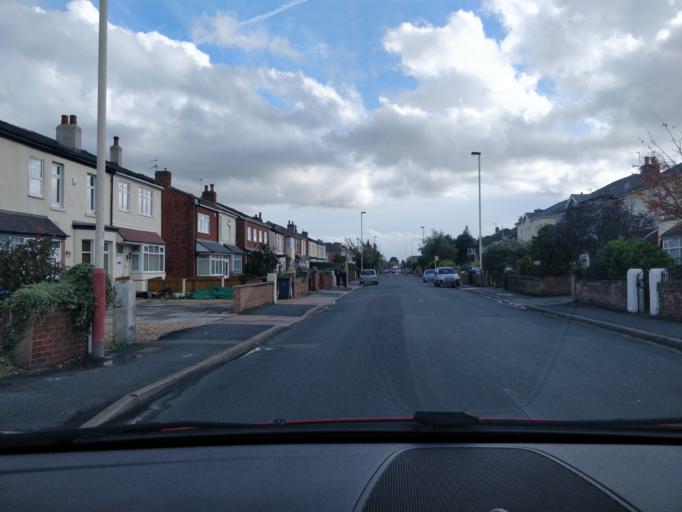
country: GB
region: England
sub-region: Sefton
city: Southport
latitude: 53.6303
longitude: -3.0081
